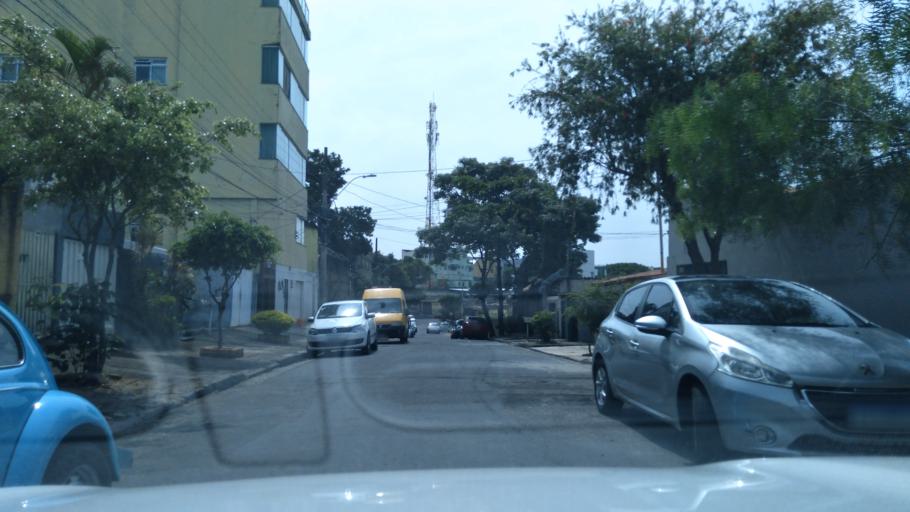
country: BR
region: Minas Gerais
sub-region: Contagem
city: Contagem
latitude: -19.8982
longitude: -44.0076
